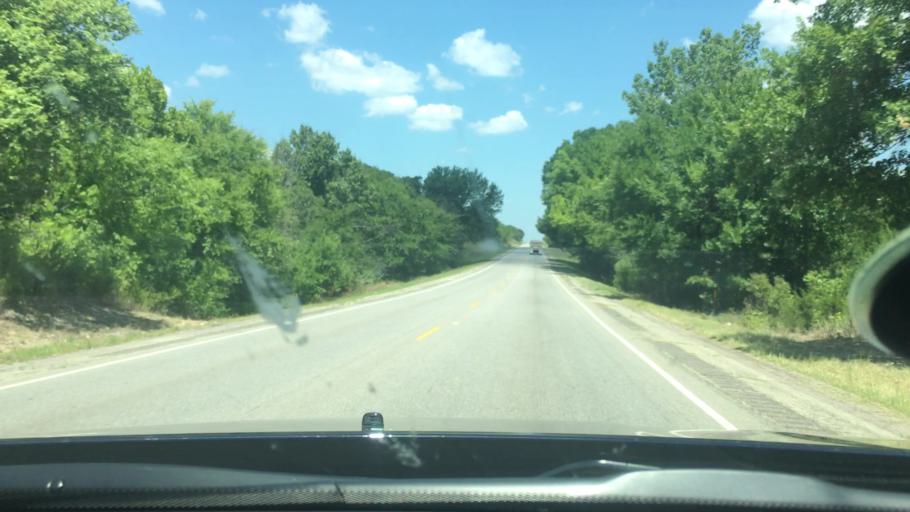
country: US
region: Oklahoma
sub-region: Marshall County
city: Oakland
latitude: 34.1487
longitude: -96.8110
